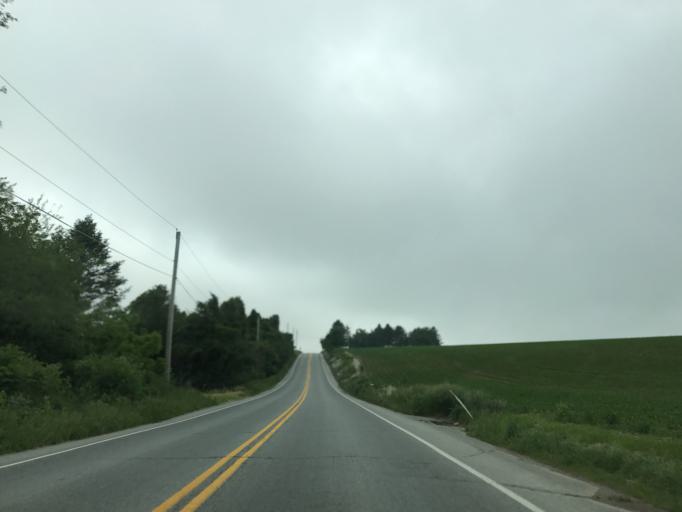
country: US
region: Pennsylvania
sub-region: York County
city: Susquehanna Trails
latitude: 39.8517
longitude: -76.4324
